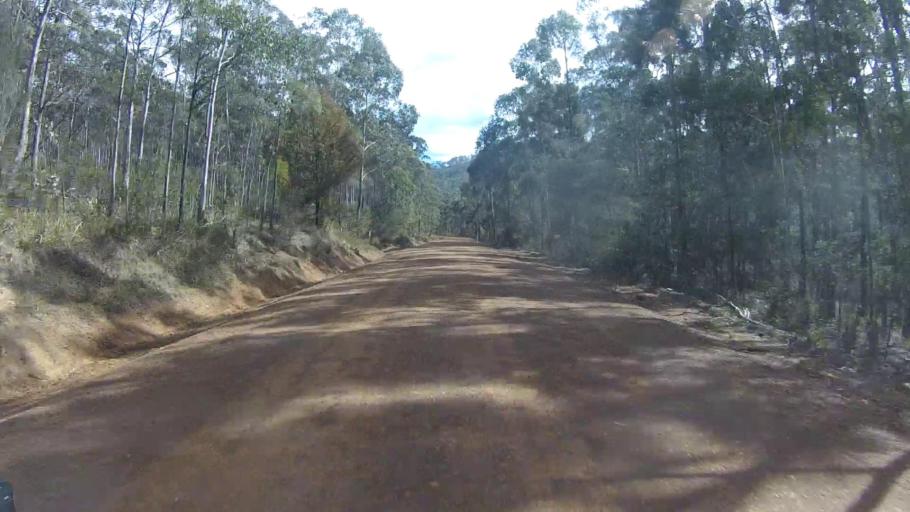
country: AU
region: Tasmania
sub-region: Sorell
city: Sorell
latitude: -42.6249
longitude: 147.9027
